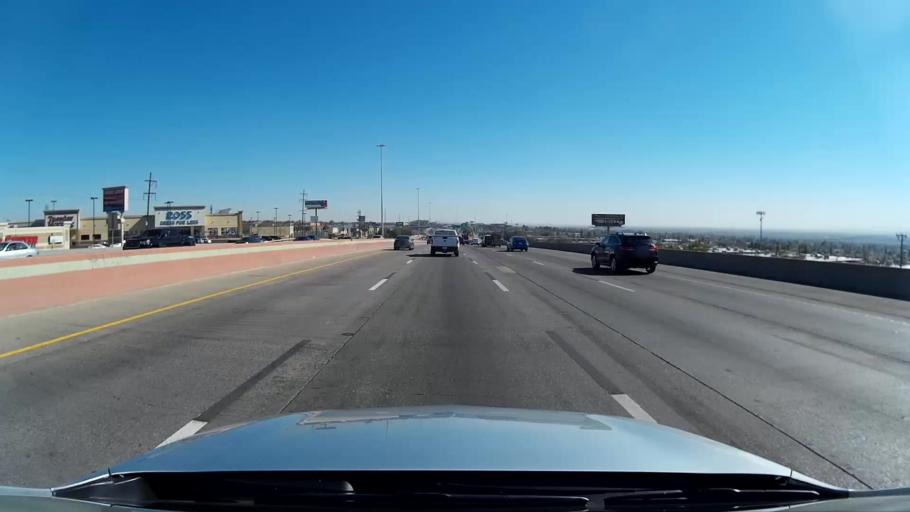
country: US
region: Texas
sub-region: El Paso County
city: Fort Bliss
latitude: 31.7638
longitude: -106.3637
